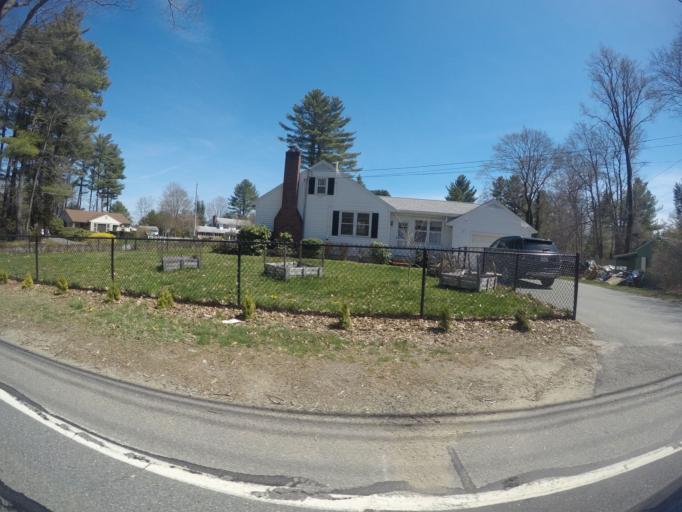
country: US
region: Massachusetts
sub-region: Bristol County
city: Easton
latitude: 42.0437
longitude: -71.0859
